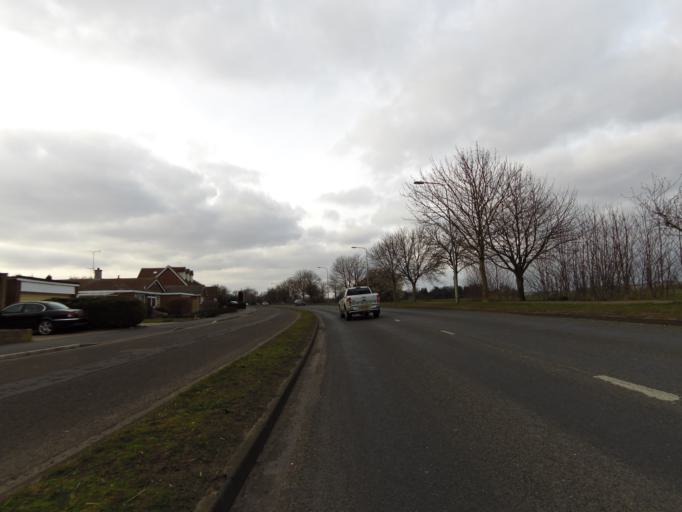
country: GB
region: England
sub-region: Suffolk
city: Ipswich
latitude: 52.0805
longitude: 1.1502
